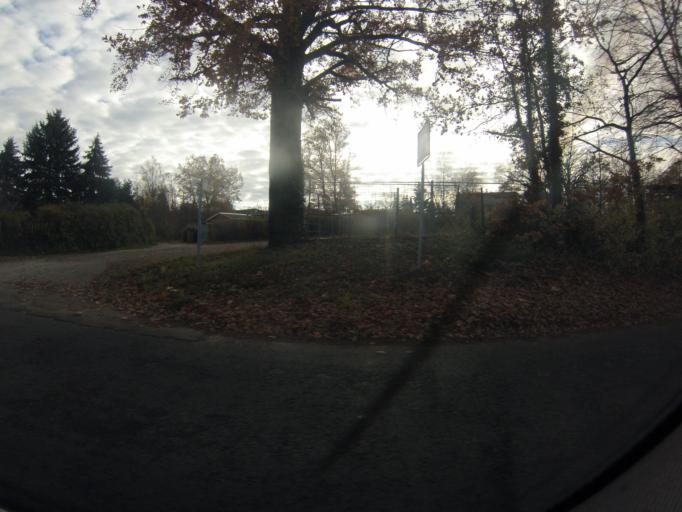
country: DE
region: Thuringia
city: Ponitz
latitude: 50.8547
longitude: 12.4422
